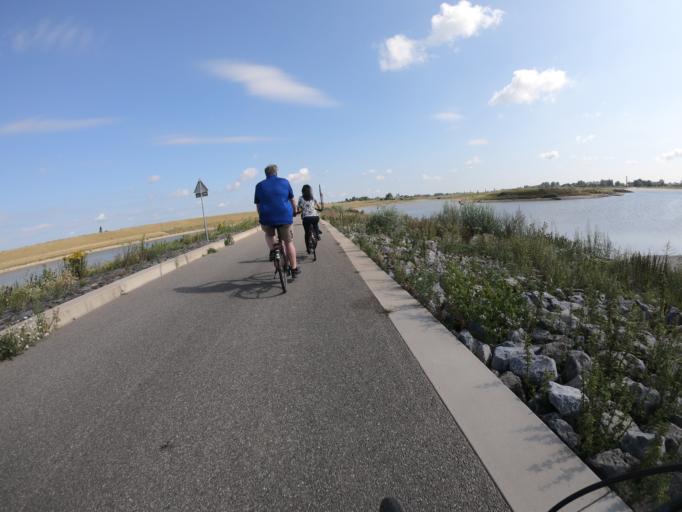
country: NL
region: Gelderland
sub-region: Gemeente Nijmegen
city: Nijmegen
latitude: 51.8570
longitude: 5.8739
